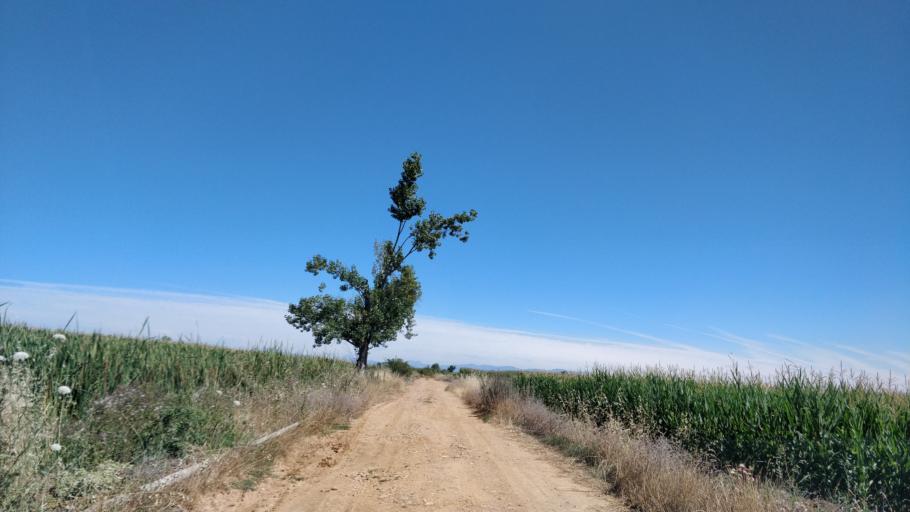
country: ES
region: Castille and Leon
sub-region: Provincia de Leon
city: Bustillo del Paramo
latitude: 42.4419
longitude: -5.8151
